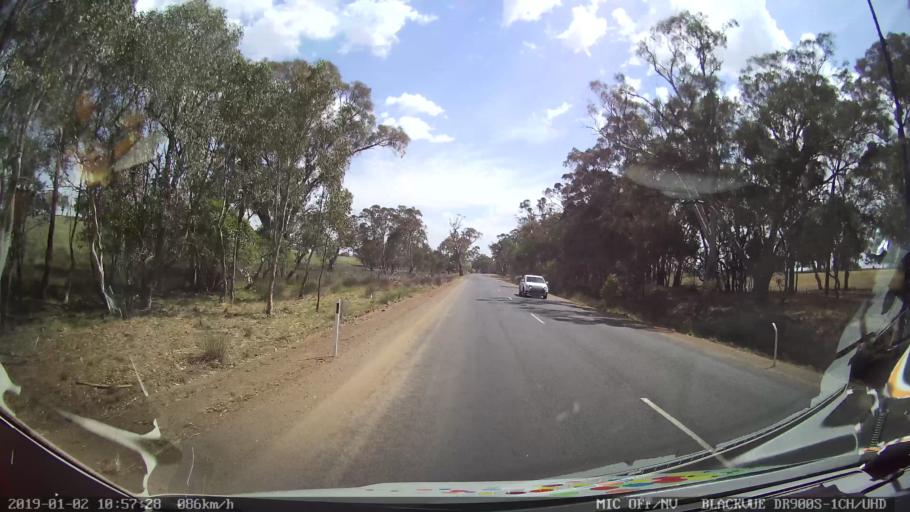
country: AU
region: New South Wales
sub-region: Cootamundra
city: Cootamundra
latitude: -34.6350
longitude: 148.2828
